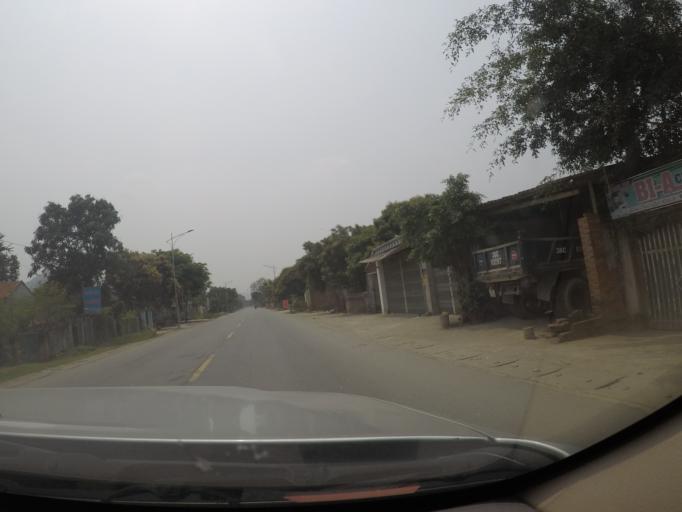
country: VN
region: Thanh Hoa
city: Thi Tran Cam Thuy
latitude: 20.2021
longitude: 105.4764
